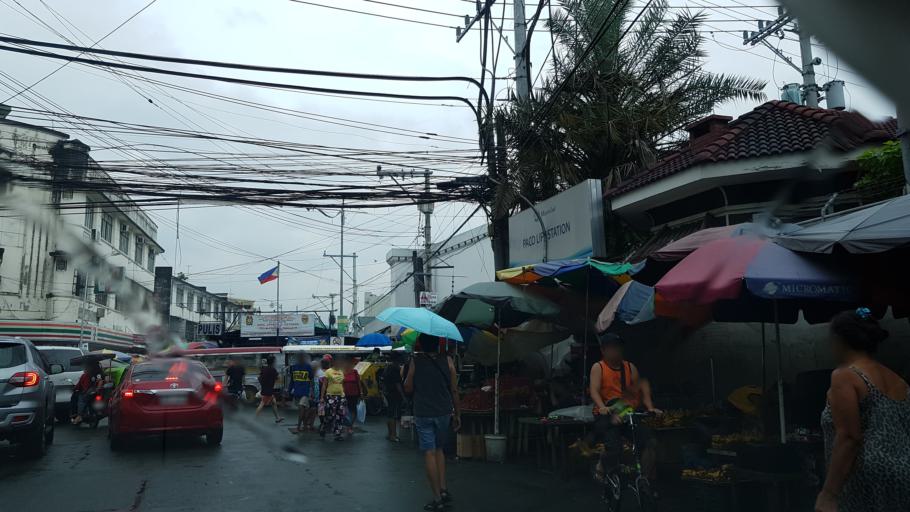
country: PH
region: Metro Manila
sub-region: City of Manila
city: Quiapo
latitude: 14.5780
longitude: 120.9934
